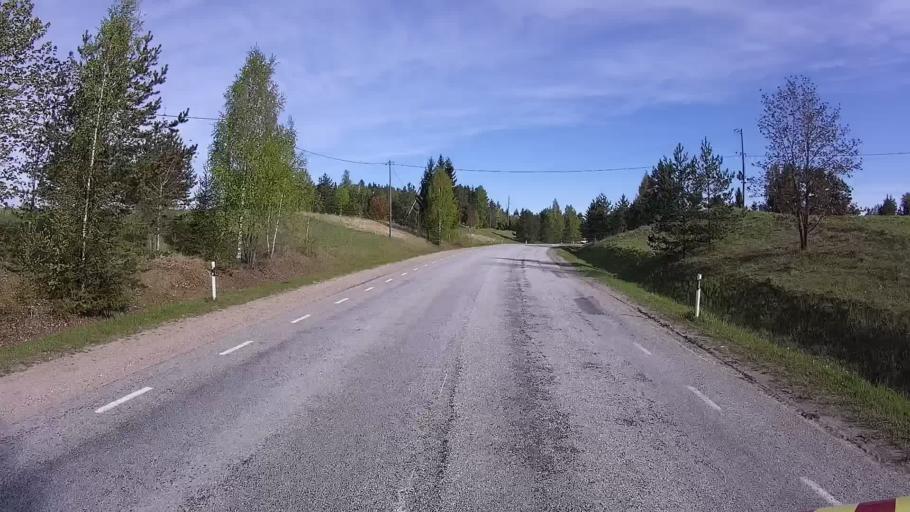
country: EE
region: Tartu
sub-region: Elva linn
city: Elva
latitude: 58.0850
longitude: 26.4919
